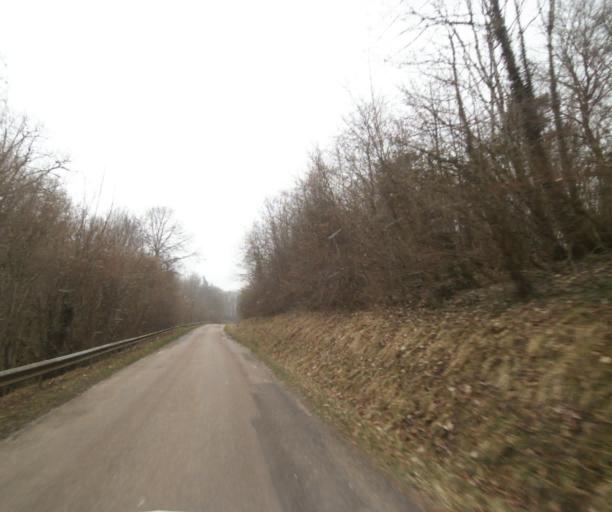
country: FR
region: Champagne-Ardenne
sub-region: Departement de la Haute-Marne
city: Chevillon
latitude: 48.5194
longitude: 5.0916
